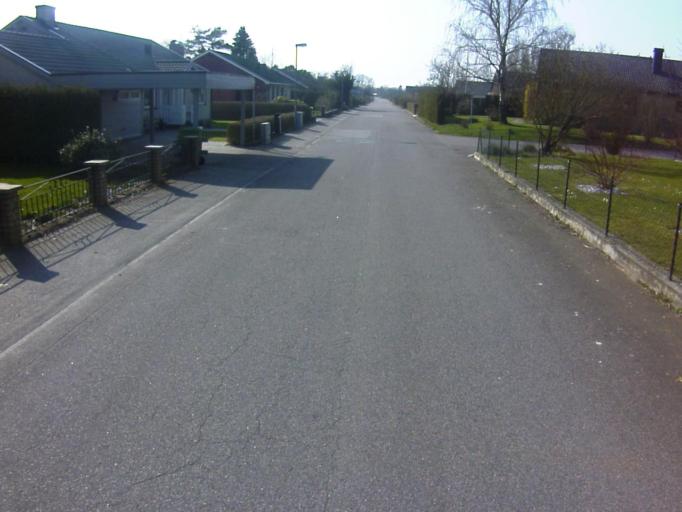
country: SE
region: Skane
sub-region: Kavlinge Kommun
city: Kaevlinge
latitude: 55.7931
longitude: 13.1430
